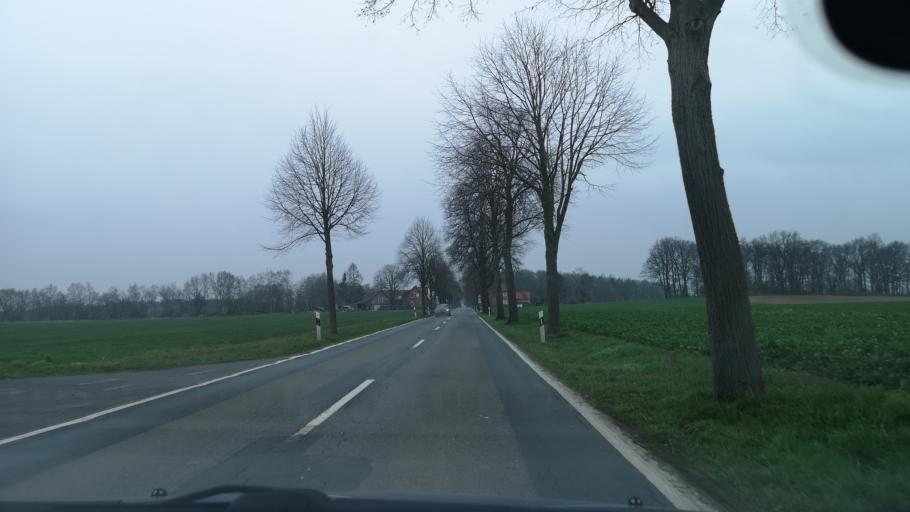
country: DE
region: Lower Saxony
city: Neustadt am Rubenberge
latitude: 52.5734
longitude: 9.4317
